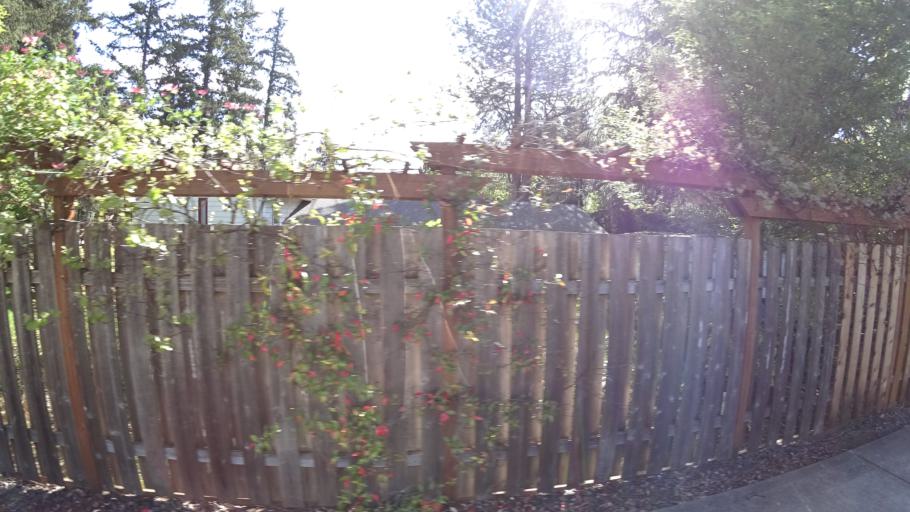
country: US
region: Oregon
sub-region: Washington County
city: King City
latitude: 45.4433
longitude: -122.8230
